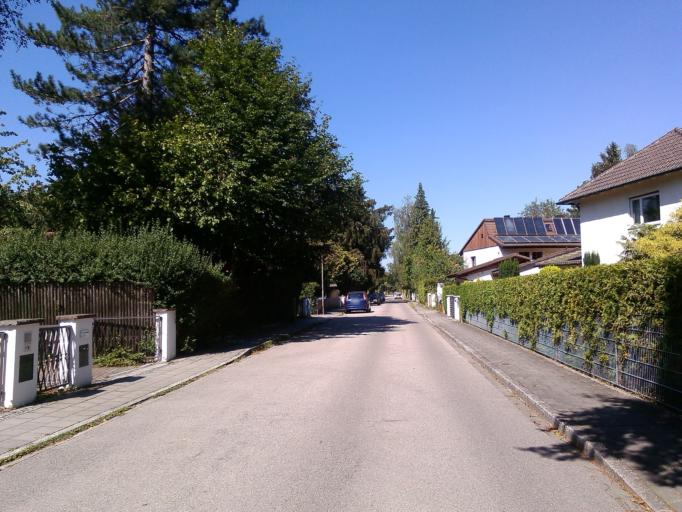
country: DE
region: Bavaria
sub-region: Upper Bavaria
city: Gauting
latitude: 48.0785
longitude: 11.3849
